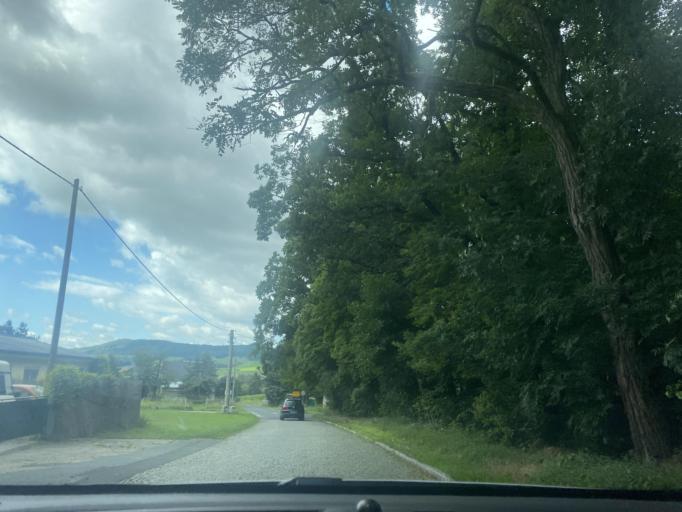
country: DE
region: Saxony
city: Reichenbach
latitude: 51.1337
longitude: 14.7906
